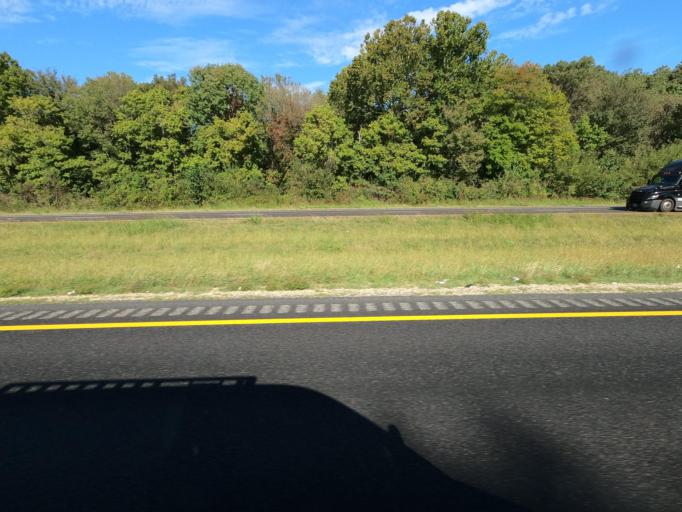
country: US
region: Tennessee
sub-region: Tipton County
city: Mason
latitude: 35.3402
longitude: -89.5368
